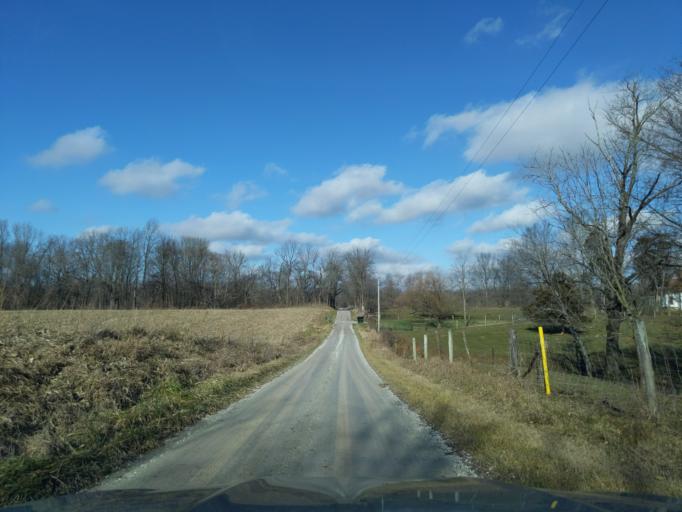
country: US
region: Indiana
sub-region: Decatur County
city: Greensburg
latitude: 39.2434
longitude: -85.4841
